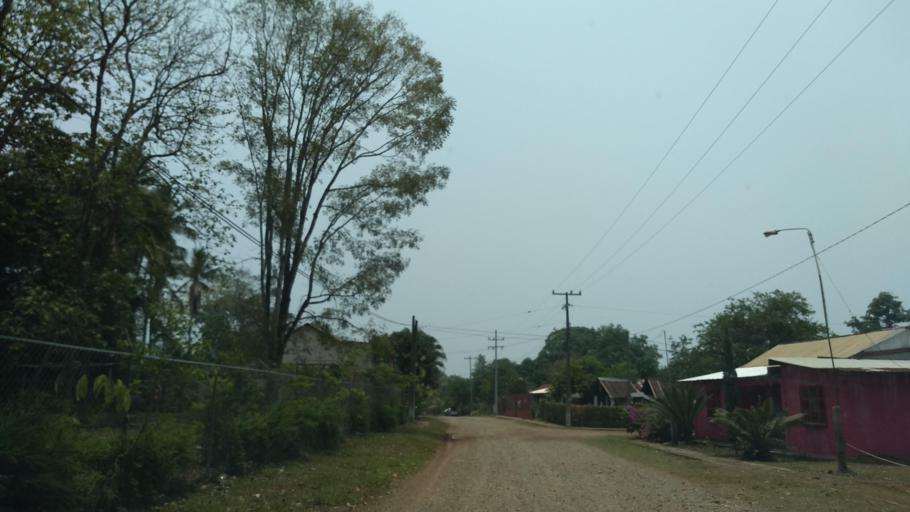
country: MX
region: Veracruz
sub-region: Tezonapa
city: Laguna Chica (Pueblo Nuevo)
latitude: 18.5150
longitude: -96.7626
